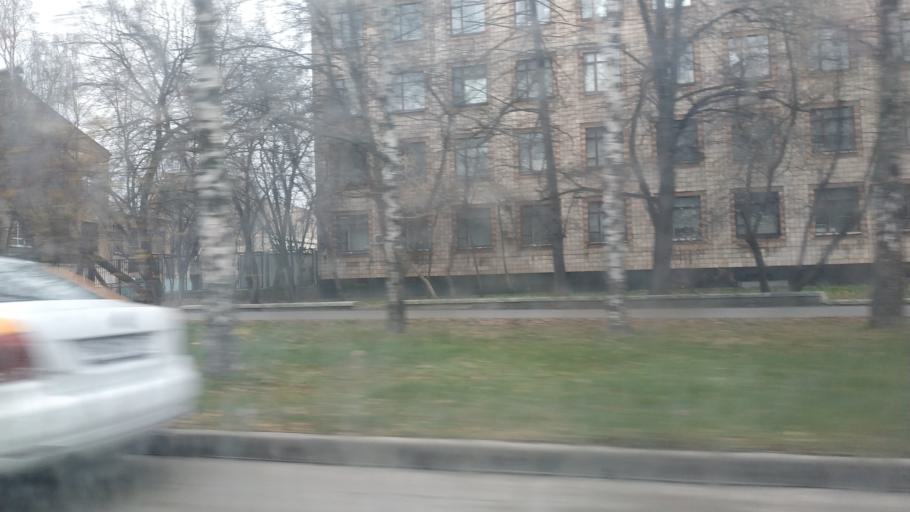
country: RU
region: Moskovskaya
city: Leninskiye Gory
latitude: 55.7000
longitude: 37.5739
